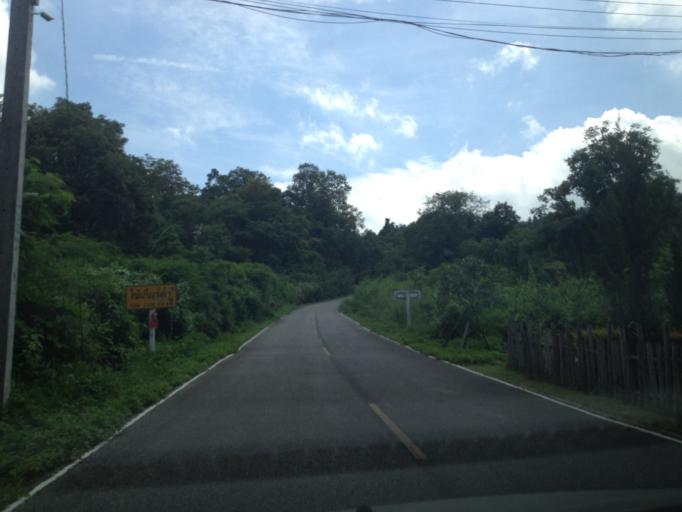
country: TH
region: Chiang Mai
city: Hang Dong
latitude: 18.7535
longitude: 98.9001
